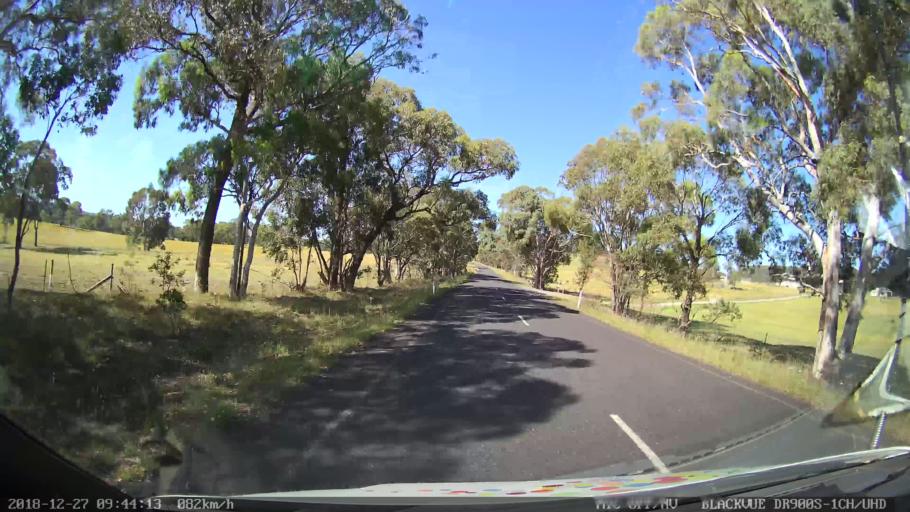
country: AU
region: New South Wales
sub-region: Lithgow
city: Portland
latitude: -33.3132
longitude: 149.9942
